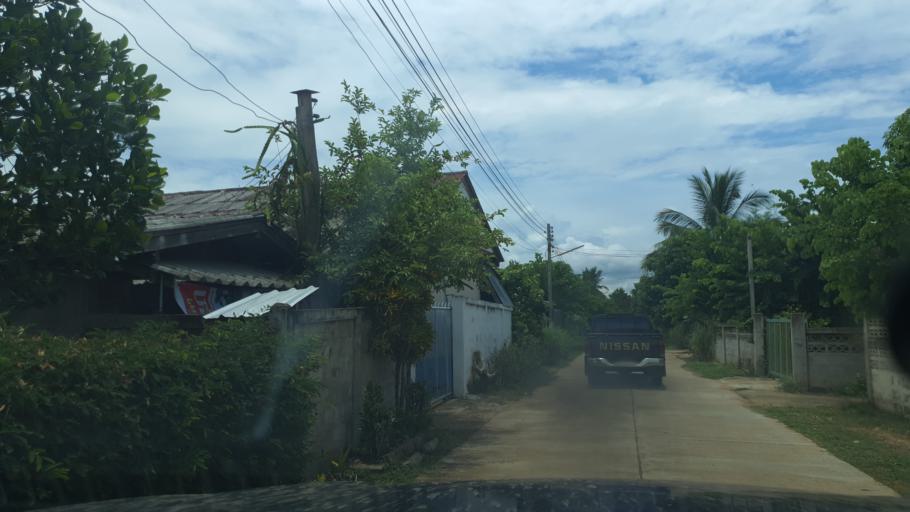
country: TH
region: Lampang
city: Soem Ngam
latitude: 18.0948
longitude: 99.3427
